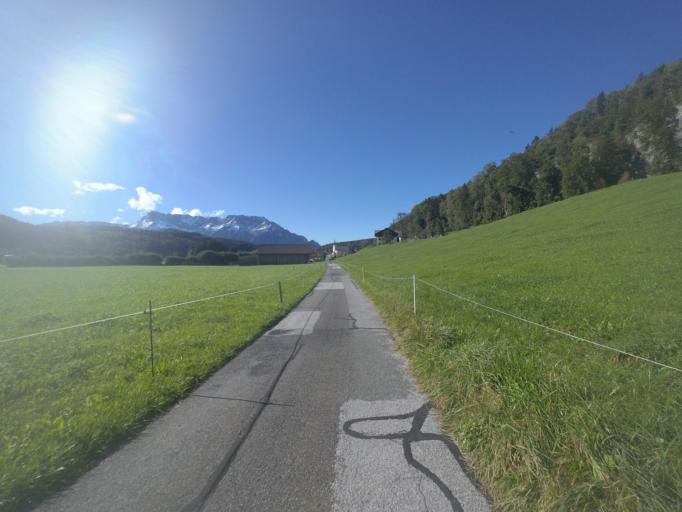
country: AT
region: Salzburg
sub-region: Politischer Bezirk Hallein
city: Adnet
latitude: 47.6927
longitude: 13.1406
